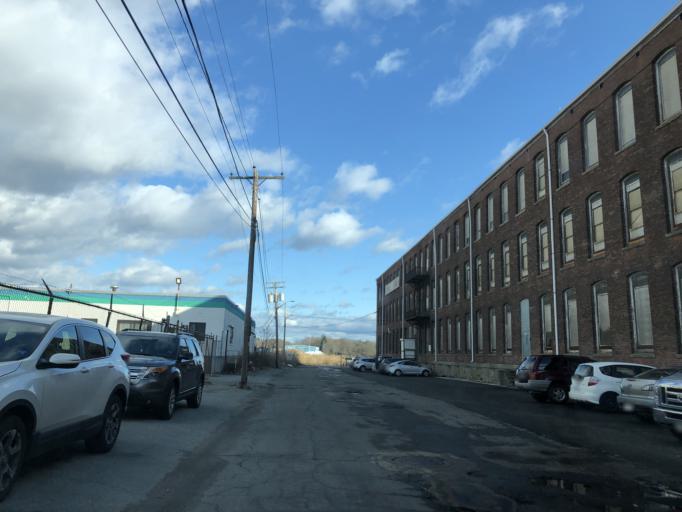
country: US
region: Massachusetts
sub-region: Bristol County
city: New Bedford
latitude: 41.6530
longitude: -70.9226
